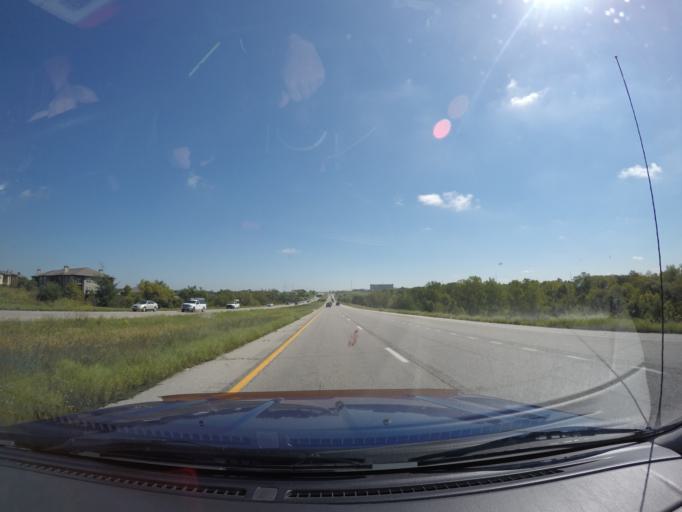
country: US
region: Kansas
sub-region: Johnson County
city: Olathe
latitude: 38.9413
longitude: -94.8113
